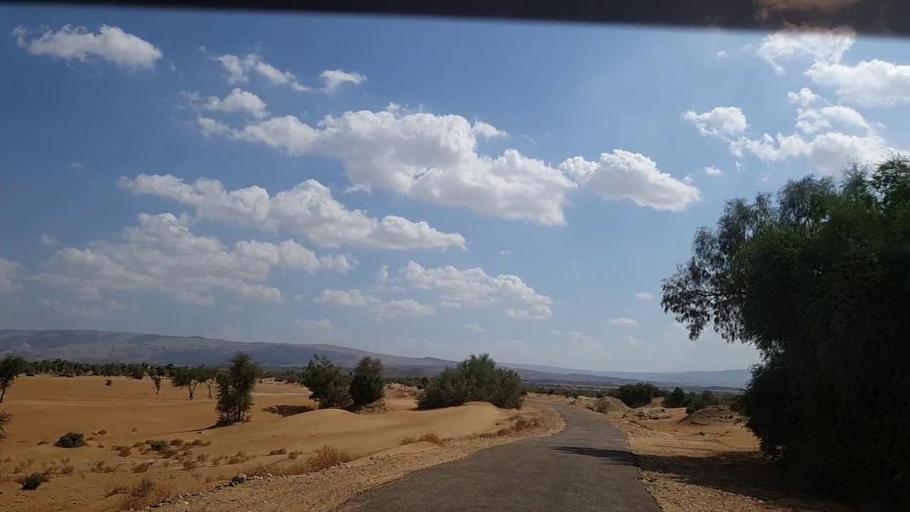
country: PK
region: Sindh
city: Johi
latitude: 26.5157
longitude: 67.4499
